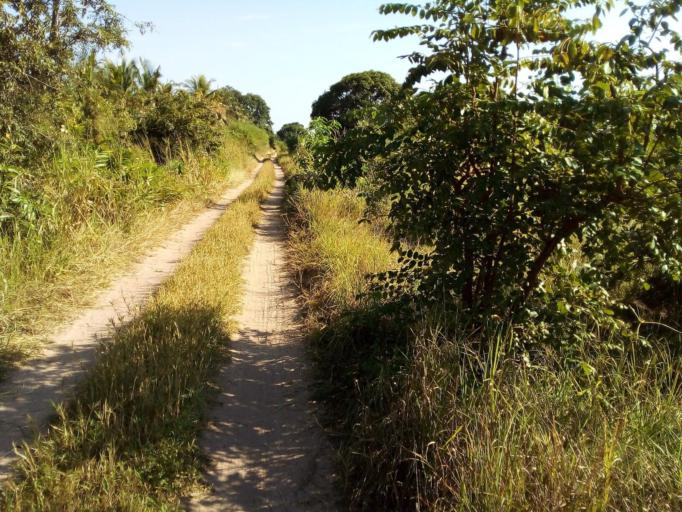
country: MZ
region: Zambezia
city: Quelimane
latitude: -17.5267
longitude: 36.8497
